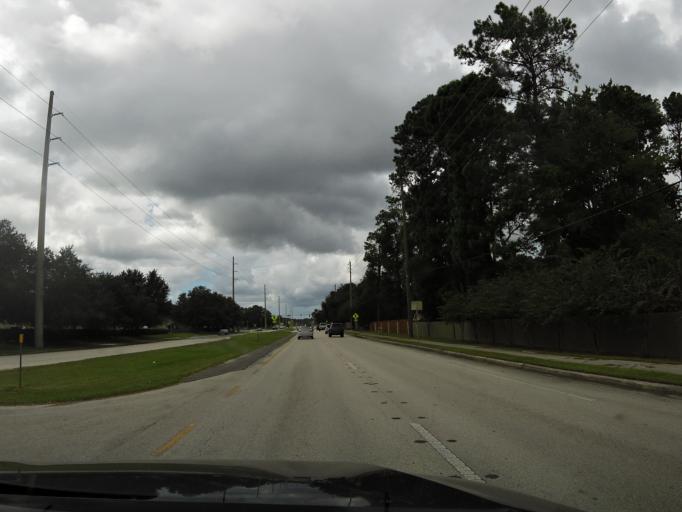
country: US
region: Florida
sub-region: Clay County
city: Lakeside
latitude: 30.1005
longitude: -81.7615
